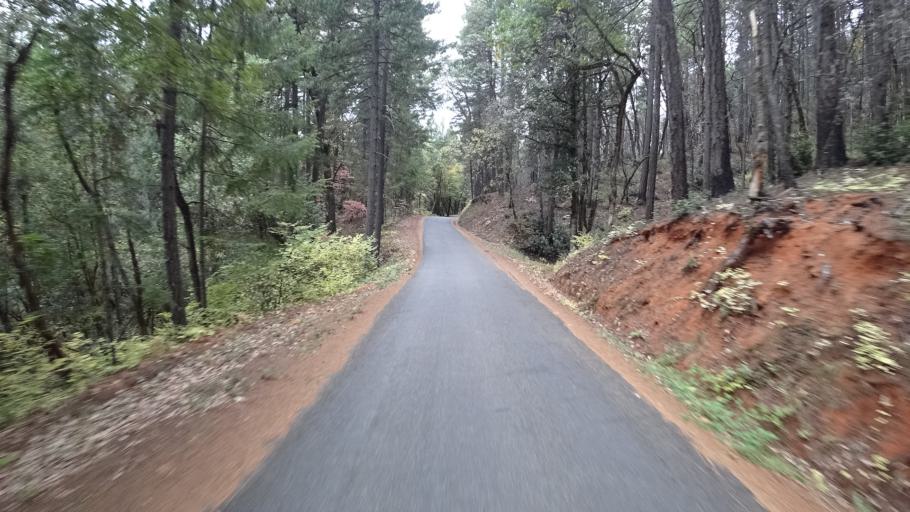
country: US
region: California
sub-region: Siskiyou County
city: Happy Camp
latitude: 41.8017
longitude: -123.3584
